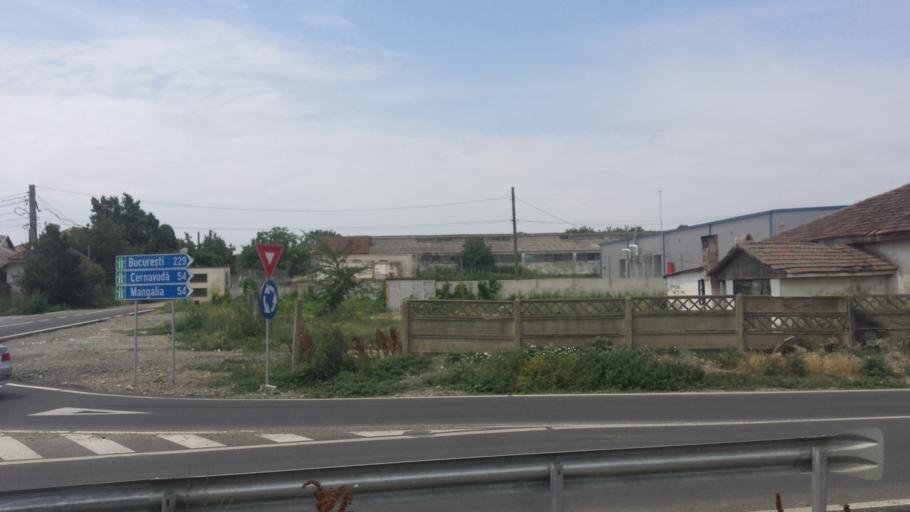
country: RO
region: Constanta
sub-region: Comuna Ovidiu
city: Ovidiu
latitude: 44.2604
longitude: 28.5541
